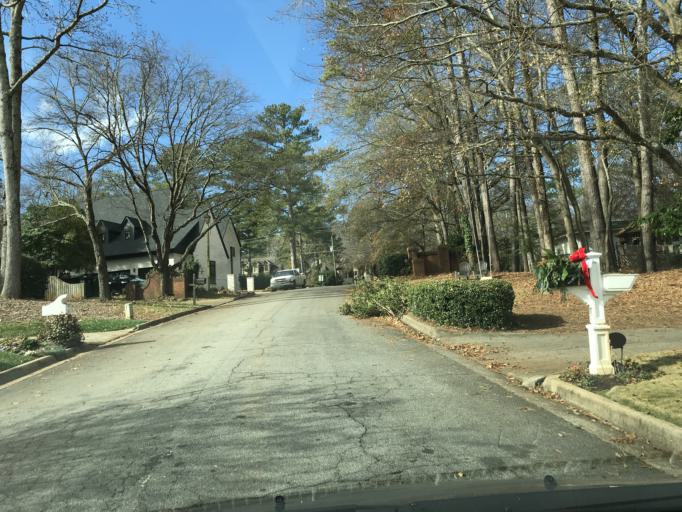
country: US
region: Georgia
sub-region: DeKalb County
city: North Atlanta
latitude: 33.8798
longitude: -84.3460
